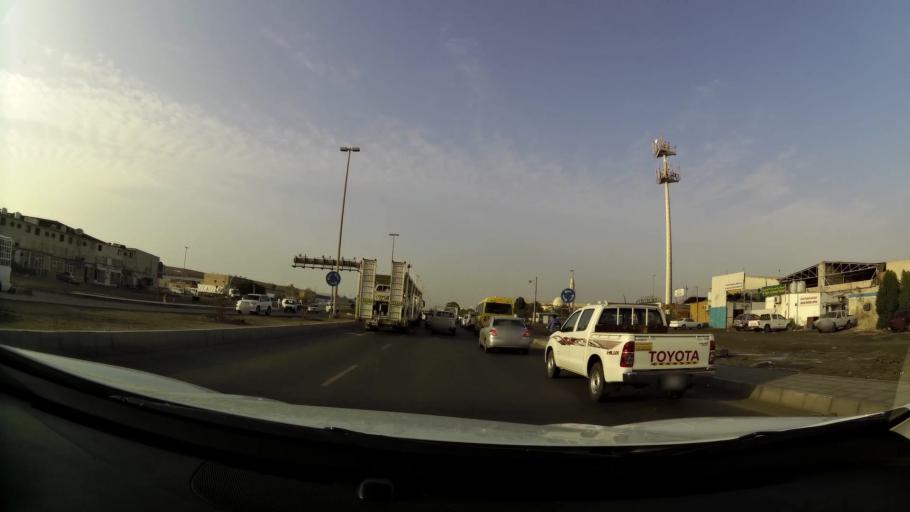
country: AE
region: Abu Dhabi
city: Abu Dhabi
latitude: 24.3584
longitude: 54.5019
